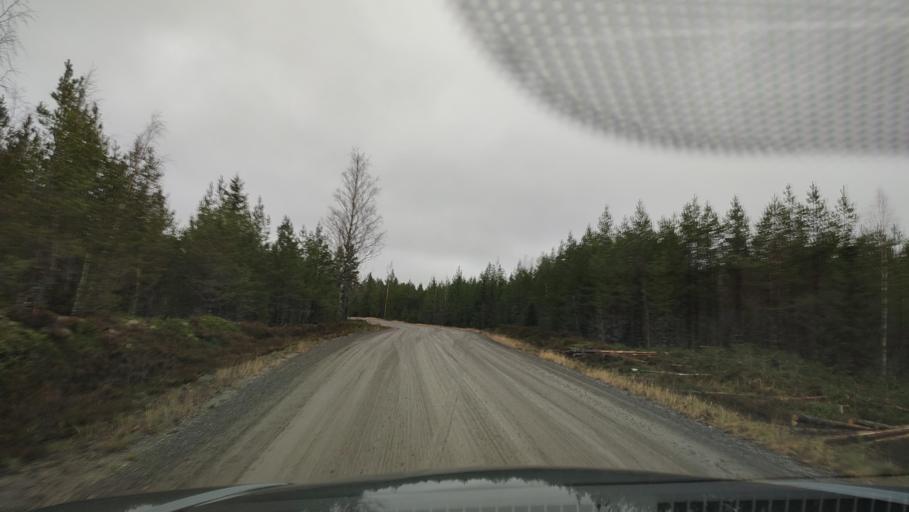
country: FI
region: Southern Ostrobothnia
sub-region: Suupohja
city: Karijoki
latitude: 62.1299
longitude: 21.6187
